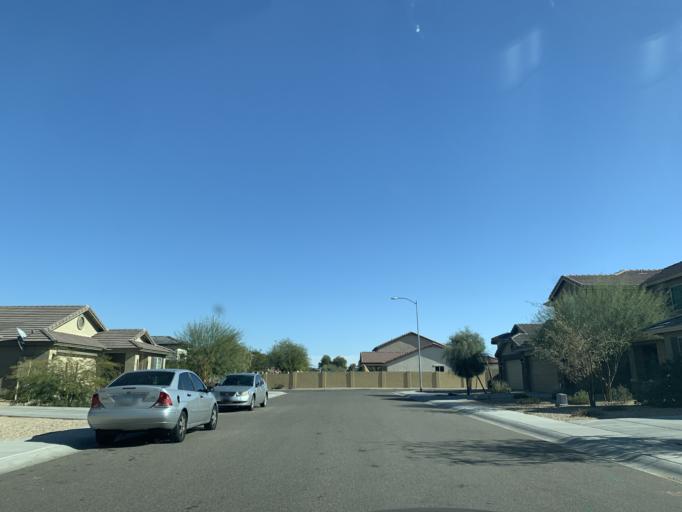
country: US
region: Arizona
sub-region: Maricopa County
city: Laveen
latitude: 33.3968
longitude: -112.1226
